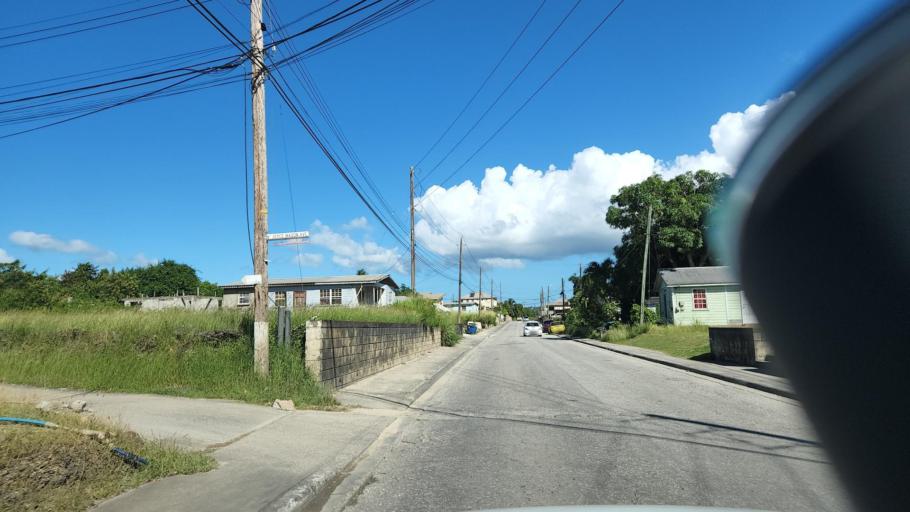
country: BB
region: Saint Thomas
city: Welchman Hall
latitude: 13.1477
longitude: -59.5995
